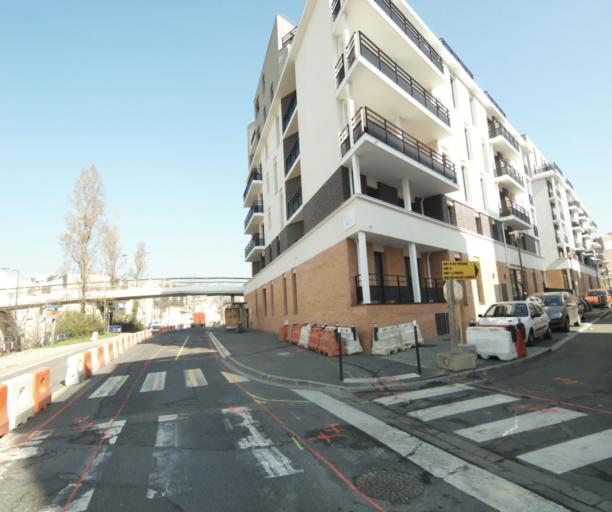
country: FR
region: Ile-de-France
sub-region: Departement du Val-d'Oise
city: Cergy
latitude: 49.0382
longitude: 2.0681
